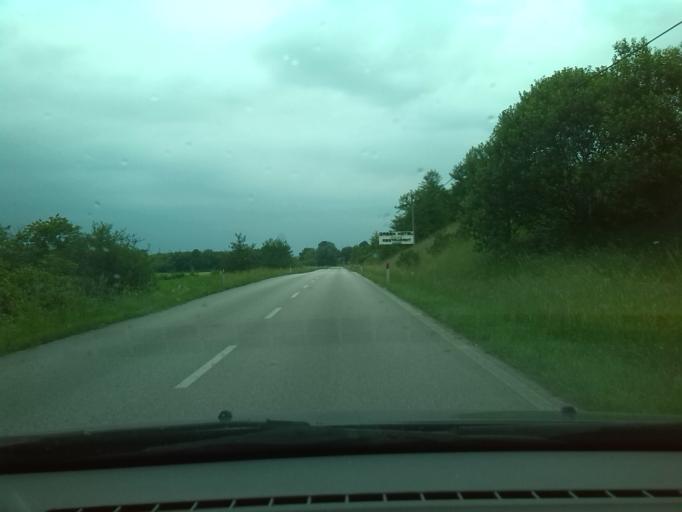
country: IT
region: Friuli Venezia Giulia
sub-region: Provincia di Udine
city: Magnano in Riviera
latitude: 46.2193
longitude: 13.1730
